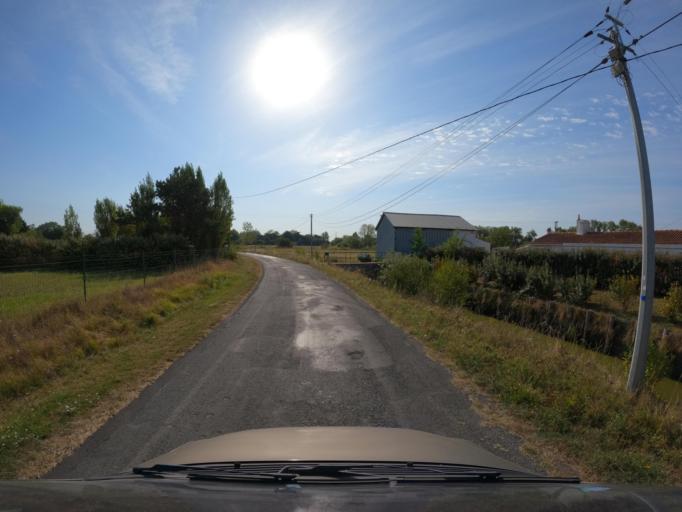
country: FR
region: Pays de la Loire
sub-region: Departement de la Vendee
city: Saint-Jean-de-Monts
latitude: 46.7983
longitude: -2.0506
